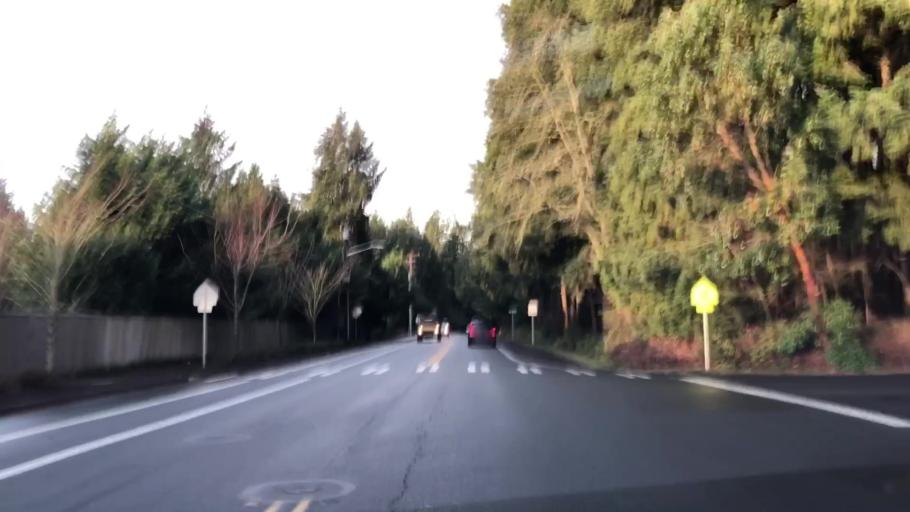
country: US
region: Washington
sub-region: King County
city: City of Sammamish
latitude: 47.6143
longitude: -122.0428
